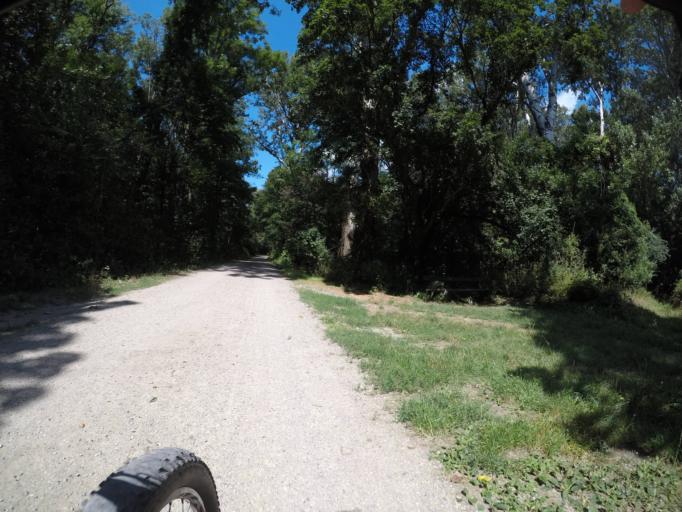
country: AT
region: Lower Austria
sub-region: Politischer Bezirk Ganserndorf
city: Gross-Enzersdorf
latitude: 48.1790
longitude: 16.5248
